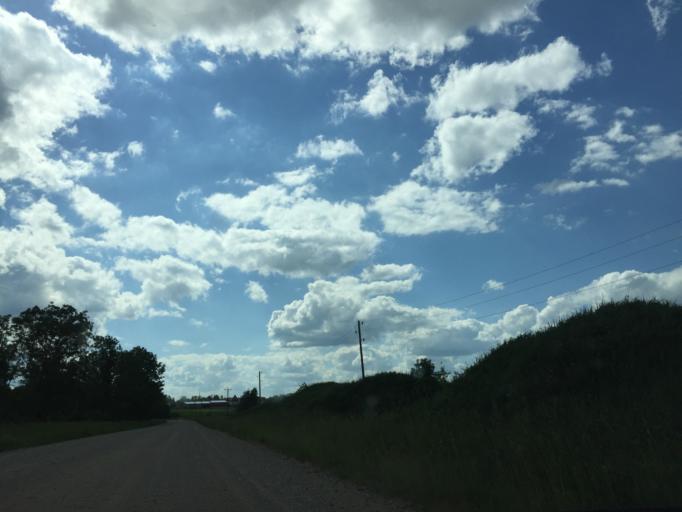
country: LV
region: Tukuma Rajons
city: Tukums
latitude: 56.9087
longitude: 23.1640
